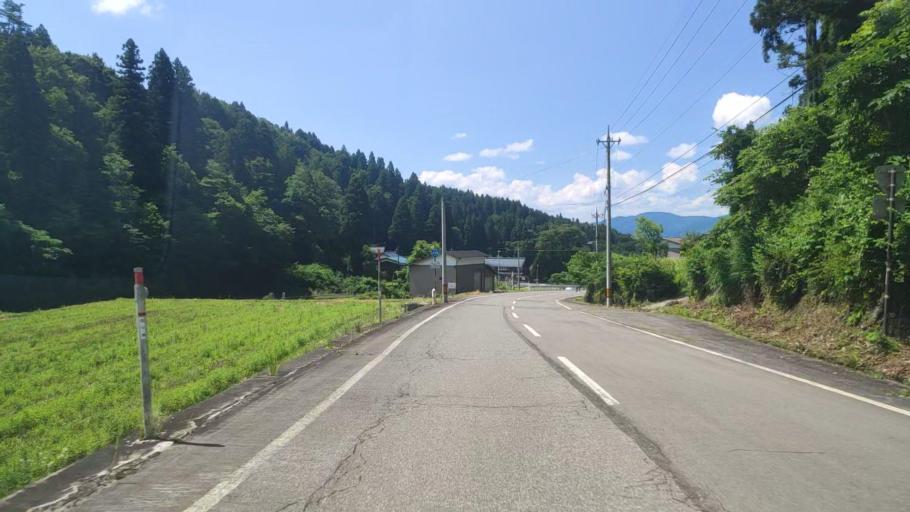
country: JP
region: Fukui
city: Katsuyama
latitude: 36.1077
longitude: 136.4976
